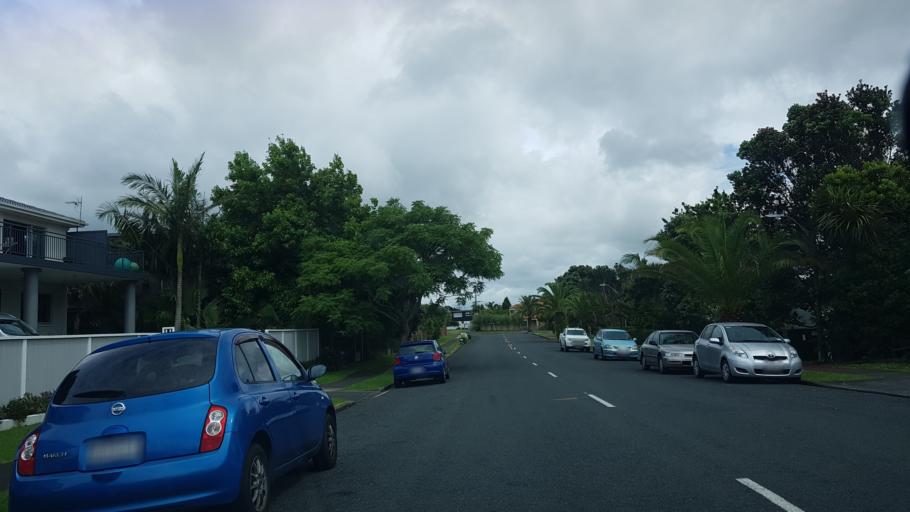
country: NZ
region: Auckland
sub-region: Auckland
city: Rosebank
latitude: -36.8308
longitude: 174.6579
